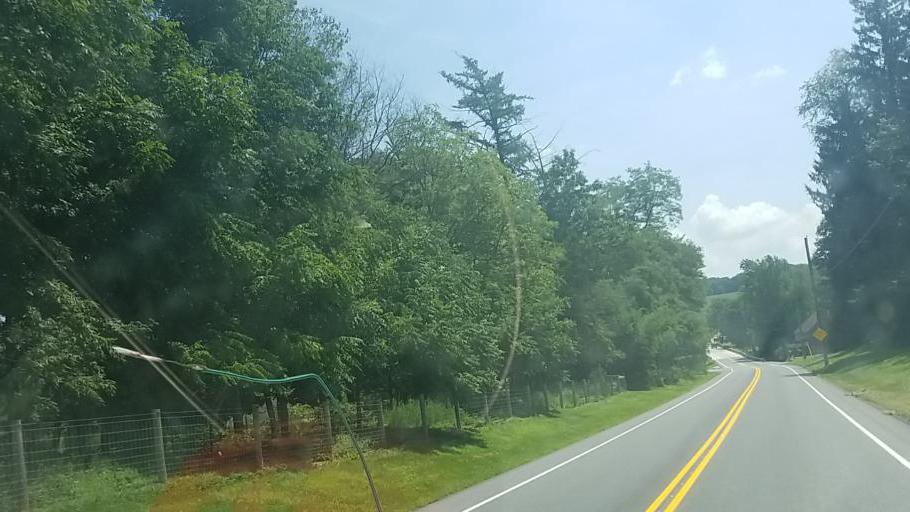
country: US
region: Pennsylvania
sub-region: Lancaster County
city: Christiana
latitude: 39.8719
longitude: -76.0062
